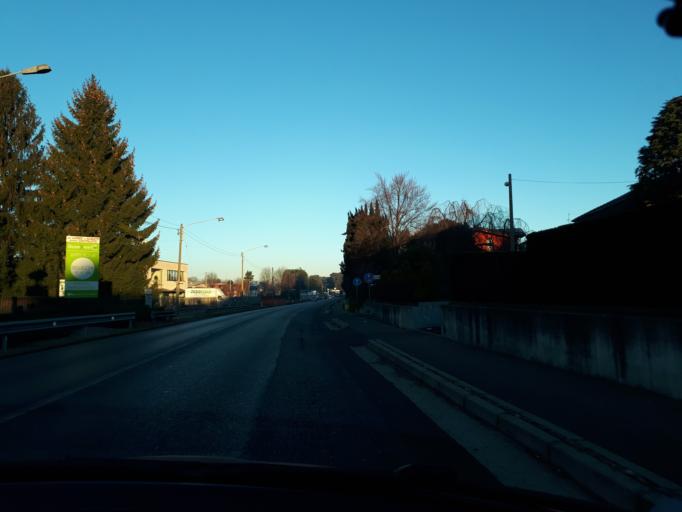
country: IT
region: Lombardy
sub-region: Provincia di Como
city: Vertemate Con Minoprio
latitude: 45.7195
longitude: 9.0734
